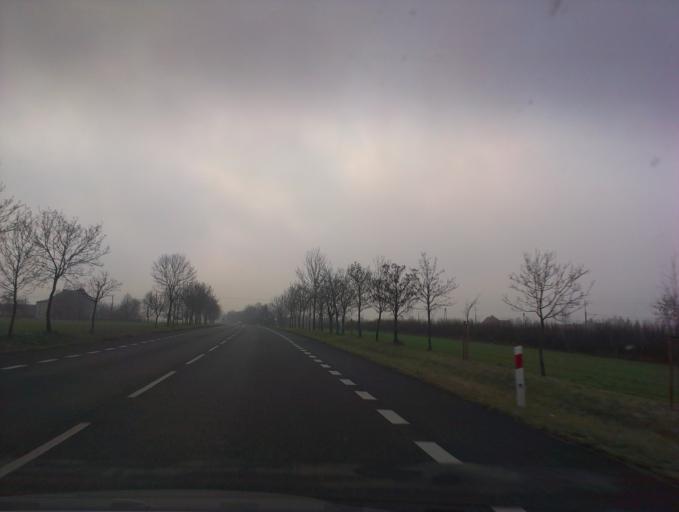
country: PL
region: Greater Poland Voivodeship
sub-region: Powiat chodzieski
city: Budzyn
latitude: 52.8856
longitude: 16.9702
